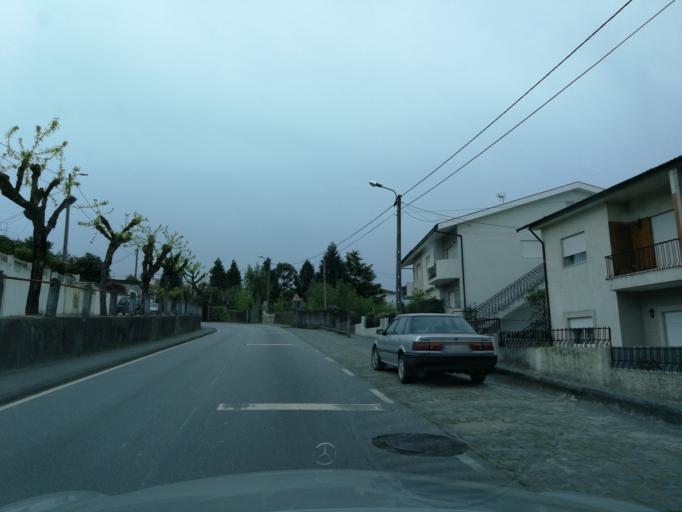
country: PT
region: Braga
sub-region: Braga
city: Braga
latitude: 41.5549
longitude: -8.4416
